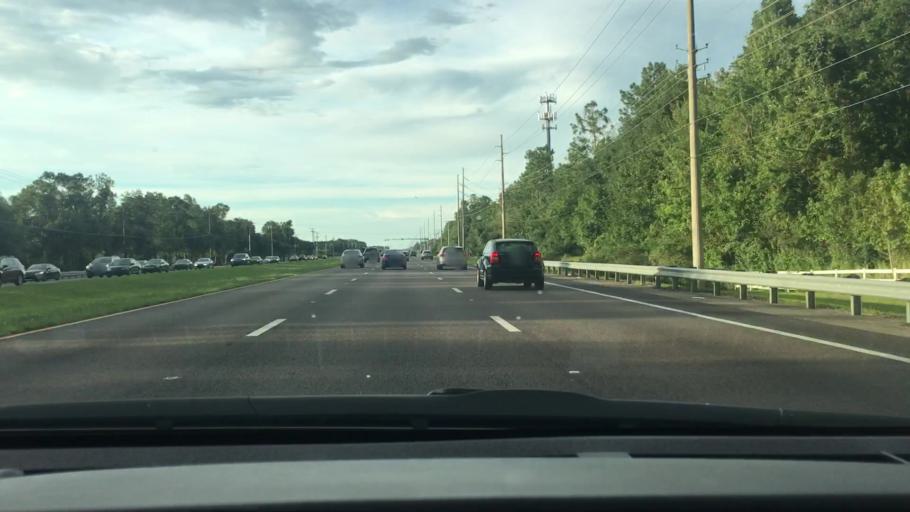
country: US
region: Florida
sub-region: Hillsborough County
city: Pebble Creek
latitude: 28.1779
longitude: -82.3535
